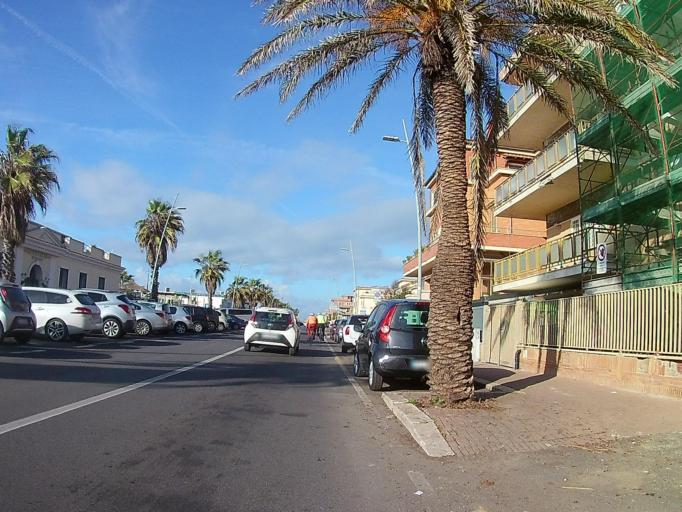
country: IT
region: Latium
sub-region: Citta metropolitana di Roma Capitale
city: Lido di Ostia
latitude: 41.7324
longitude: 12.2683
